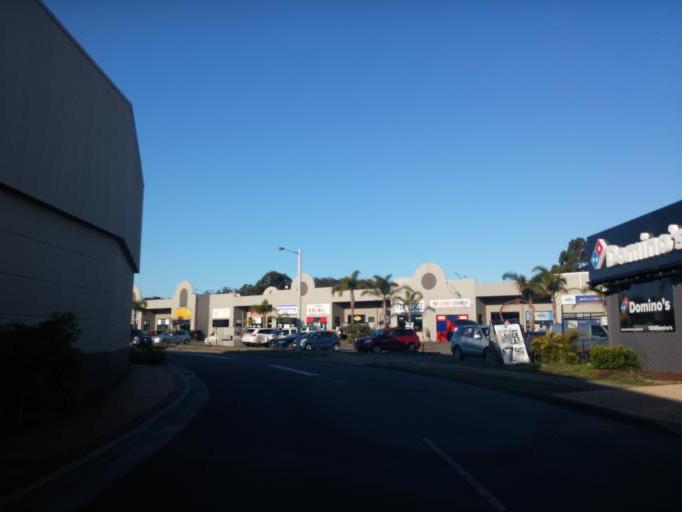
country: AU
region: New South Wales
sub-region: Port Stephens Shire
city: Corlette
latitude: -32.7368
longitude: 152.1080
